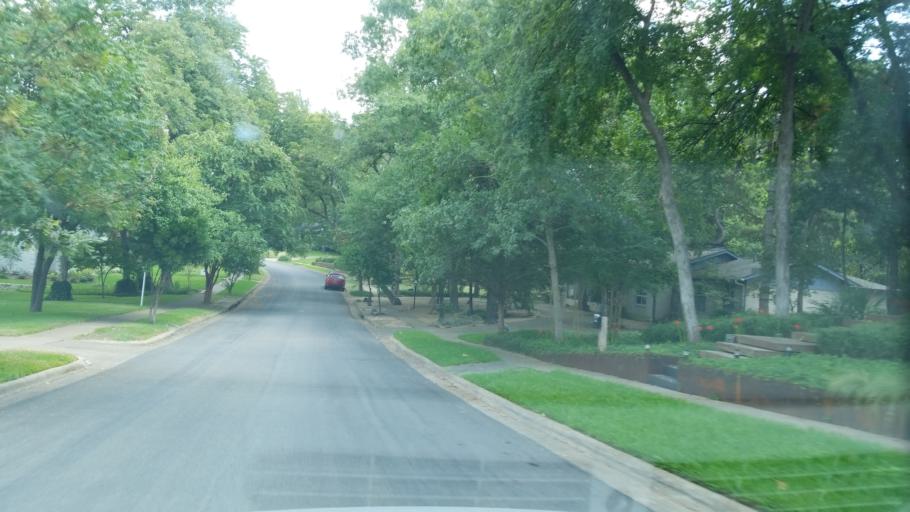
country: US
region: Texas
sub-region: Dallas County
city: Cockrell Hill
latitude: 32.7544
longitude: -96.8499
